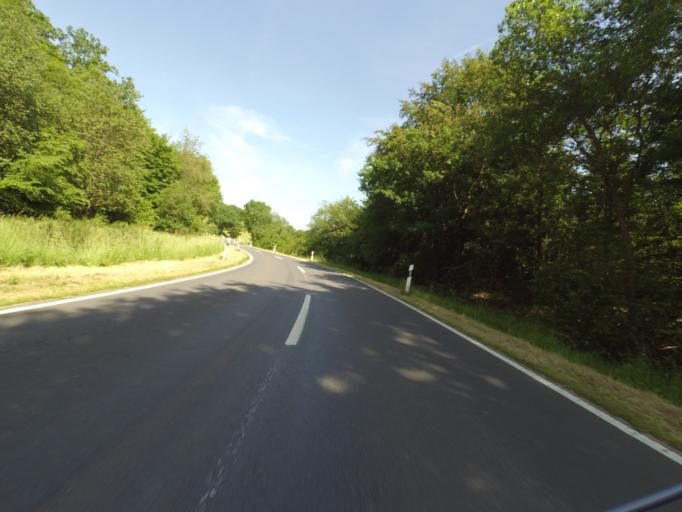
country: DE
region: Rheinland-Pfalz
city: Kaisersesch
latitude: 50.2184
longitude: 7.1513
